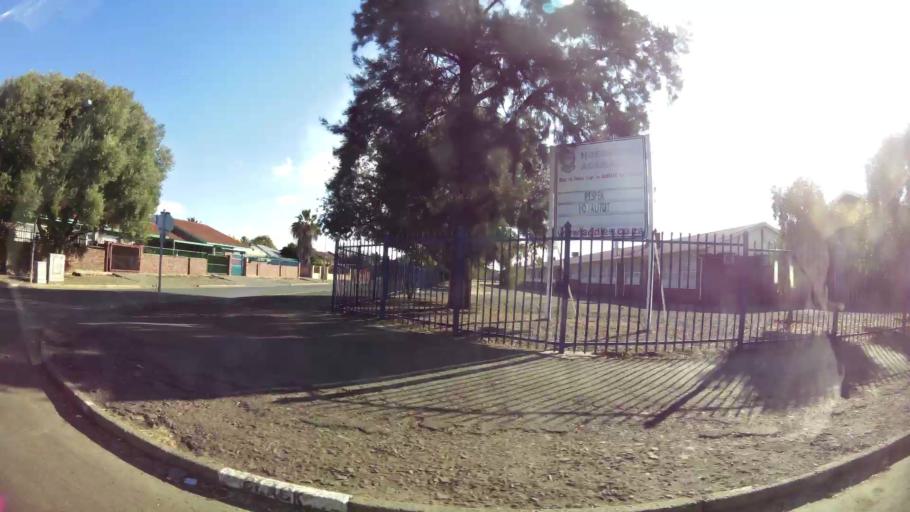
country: ZA
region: Northern Cape
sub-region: Frances Baard District Municipality
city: Kimberley
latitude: -28.7481
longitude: 24.7589
